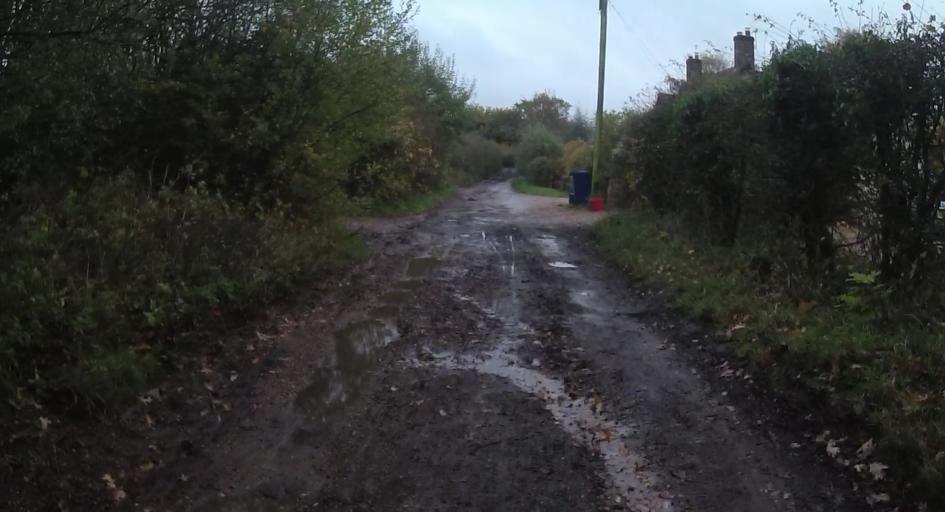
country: GB
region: England
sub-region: Surrey
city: Farnham
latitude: 51.2249
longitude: -0.8101
